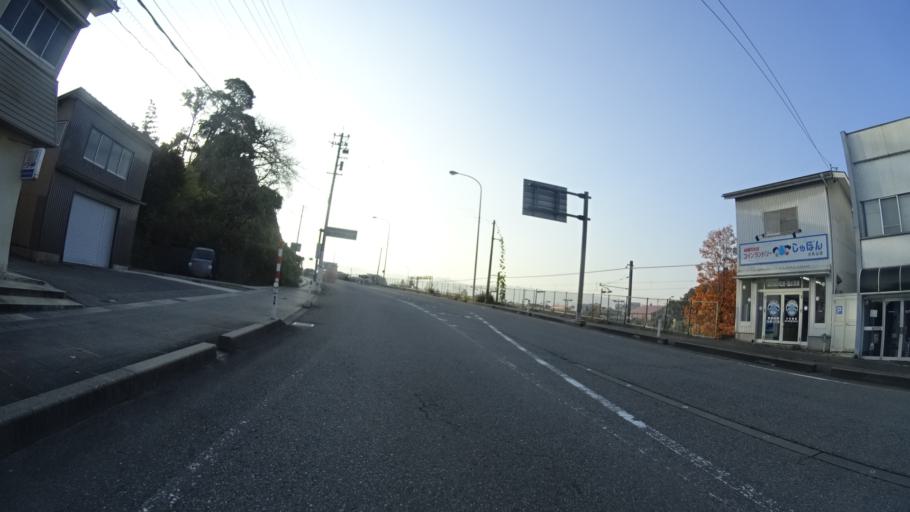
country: JP
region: Ishikawa
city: Nanao
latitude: 37.0475
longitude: 136.9576
